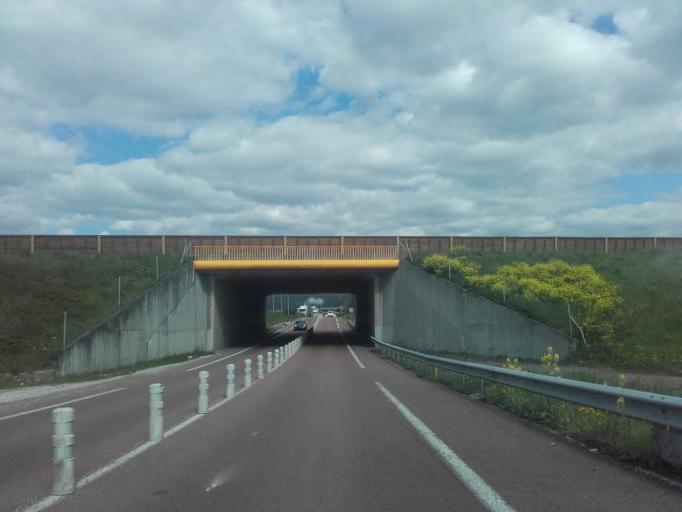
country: FR
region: Bourgogne
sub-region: Departement de la Cote-d'Or
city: Nuits-Saint-Georges
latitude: 47.1284
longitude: 4.9719
